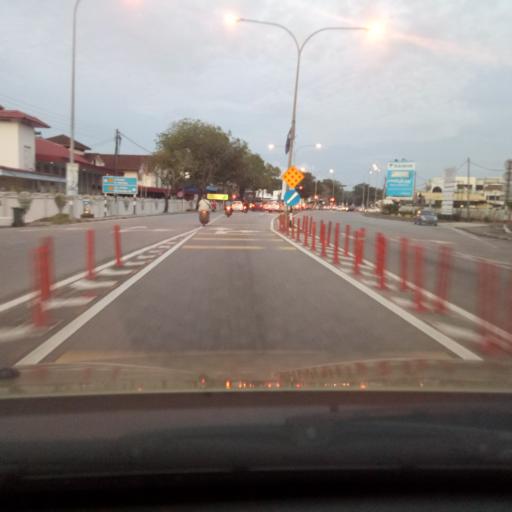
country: MY
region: Kedah
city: Alor Setar
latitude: 6.1173
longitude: 100.3742
